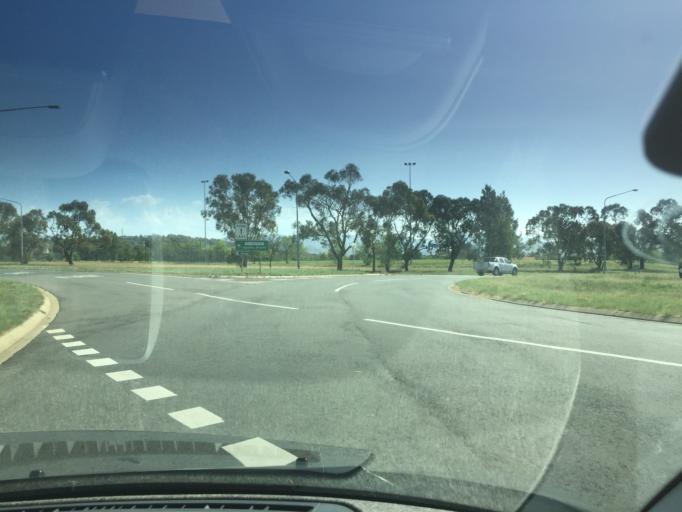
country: AU
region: Australian Capital Territory
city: Macarthur
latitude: -35.4236
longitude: 149.0902
